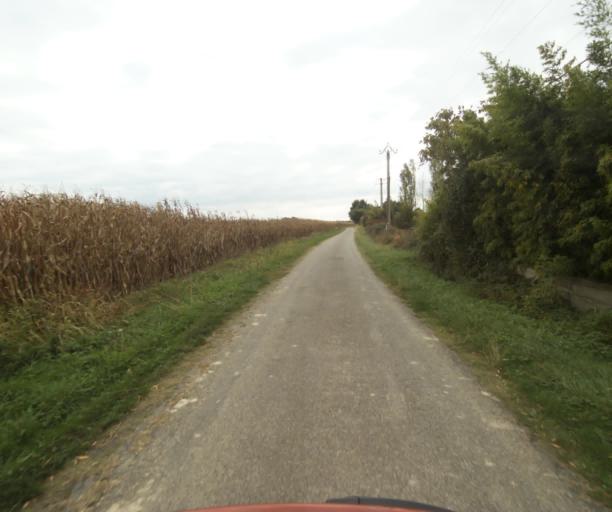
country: FR
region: Midi-Pyrenees
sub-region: Departement du Tarn-et-Garonne
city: Finhan
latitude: 43.8949
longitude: 1.2635
